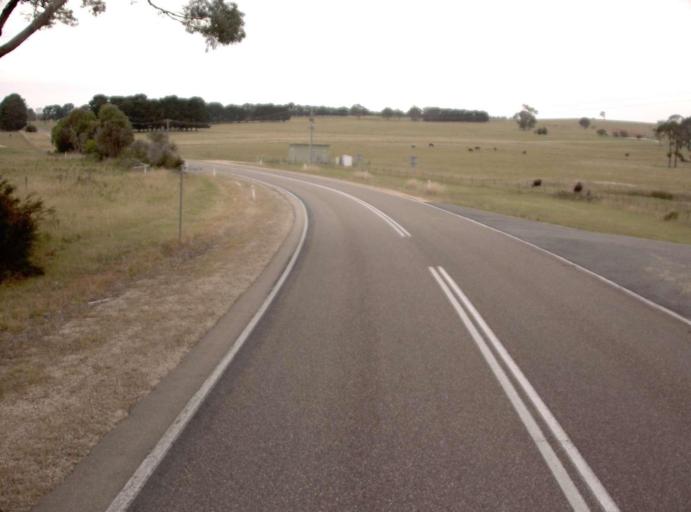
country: AU
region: Victoria
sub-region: Wellington
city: Sale
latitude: -38.1684
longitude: 147.1044
